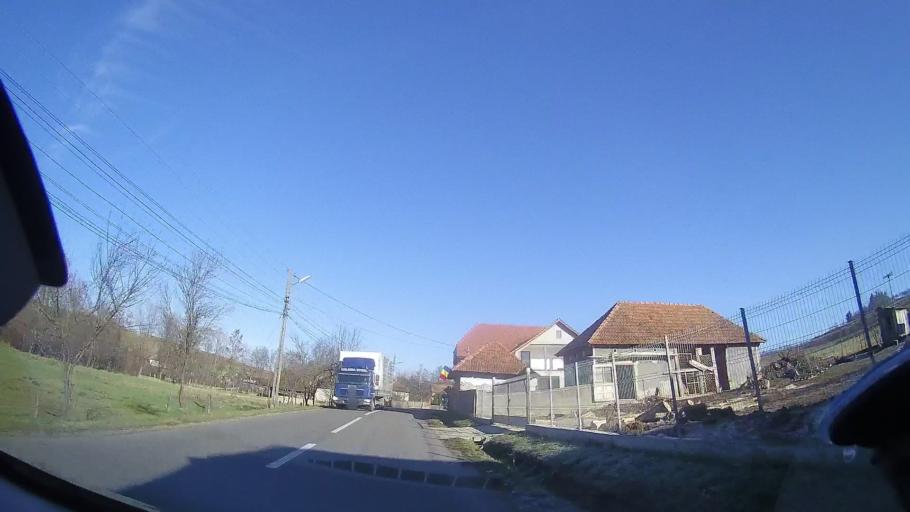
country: RO
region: Bihor
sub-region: Comuna Bratca
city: Bratca
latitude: 46.9452
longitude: 22.6073
